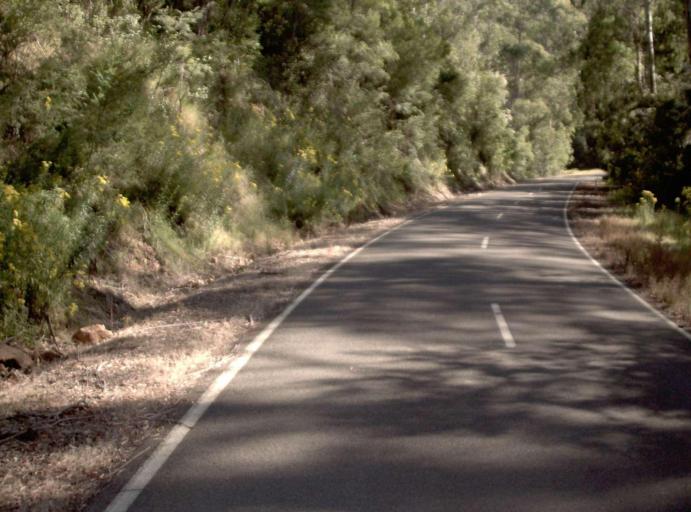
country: AU
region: Victoria
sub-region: East Gippsland
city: Lakes Entrance
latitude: -37.5258
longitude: 148.5294
